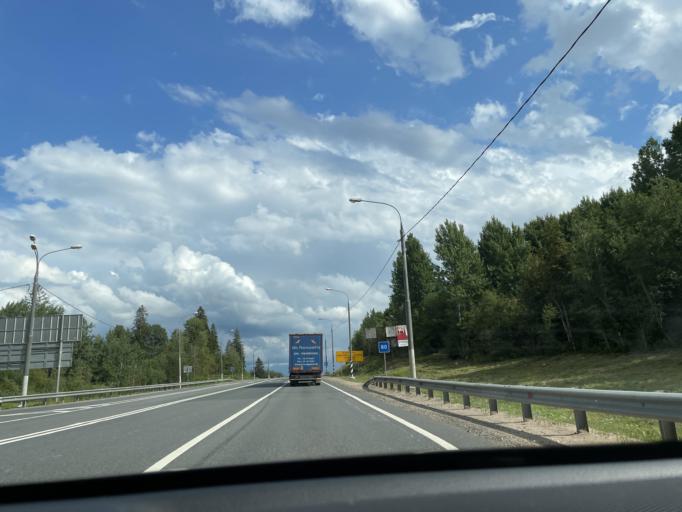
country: RU
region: Novgorod
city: Valday
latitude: 57.9504
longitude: 33.3071
